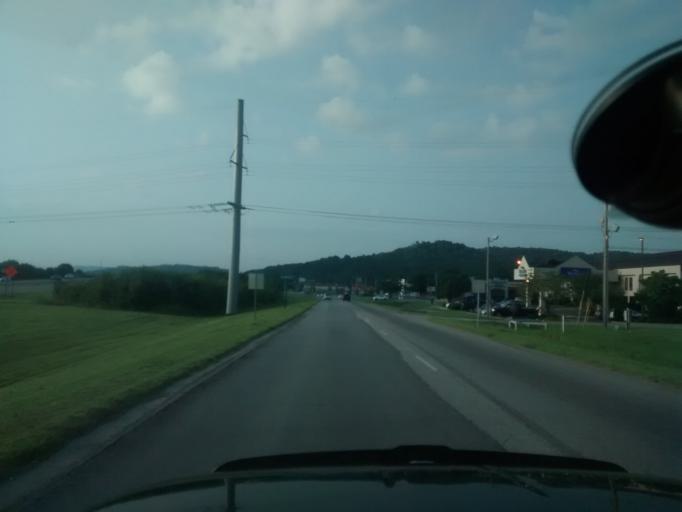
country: US
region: Arkansas
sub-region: Washington County
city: Fayetteville
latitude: 36.0570
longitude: -94.1968
